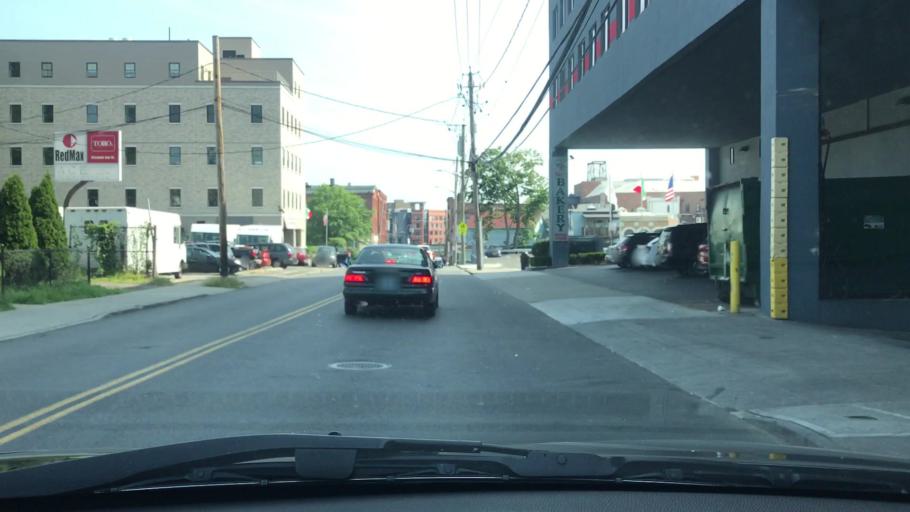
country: US
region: New York
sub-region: Westchester County
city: Port Chester
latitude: 41.0004
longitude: -73.6666
